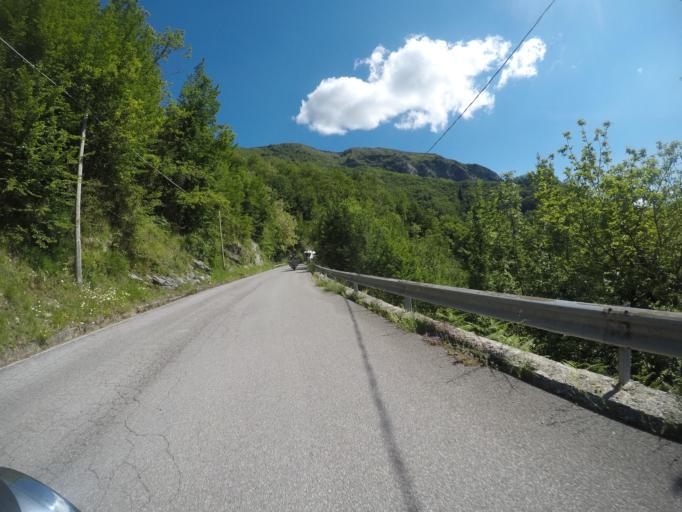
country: IT
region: Tuscany
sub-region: Provincia di Lucca
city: Fontana delle Monache
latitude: 44.0675
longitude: 10.3076
